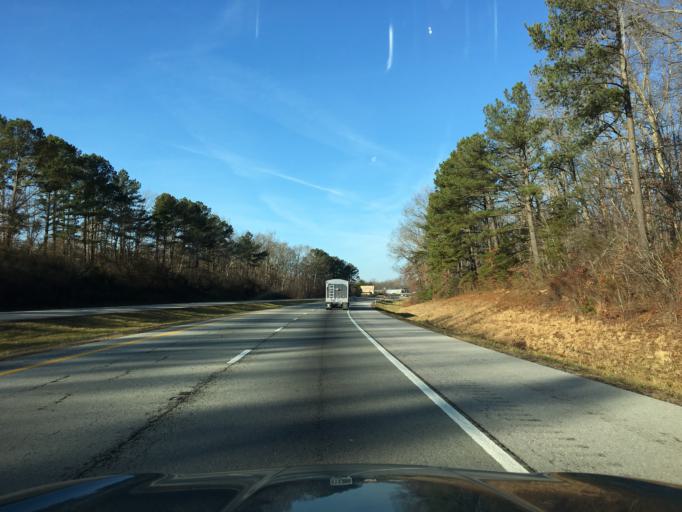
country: US
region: Tennessee
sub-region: Cumberland County
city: Crossville
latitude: 35.9577
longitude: -84.9709
